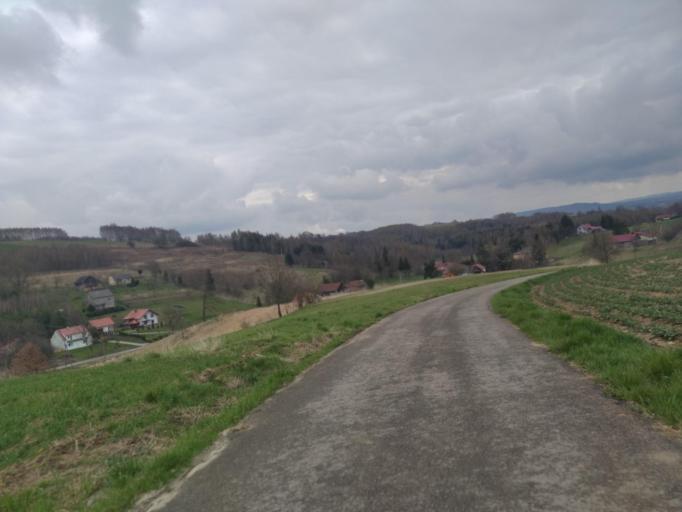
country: PL
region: Subcarpathian Voivodeship
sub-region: Powiat strzyzowski
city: Wisniowa
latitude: 49.8905
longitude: 21.7109
